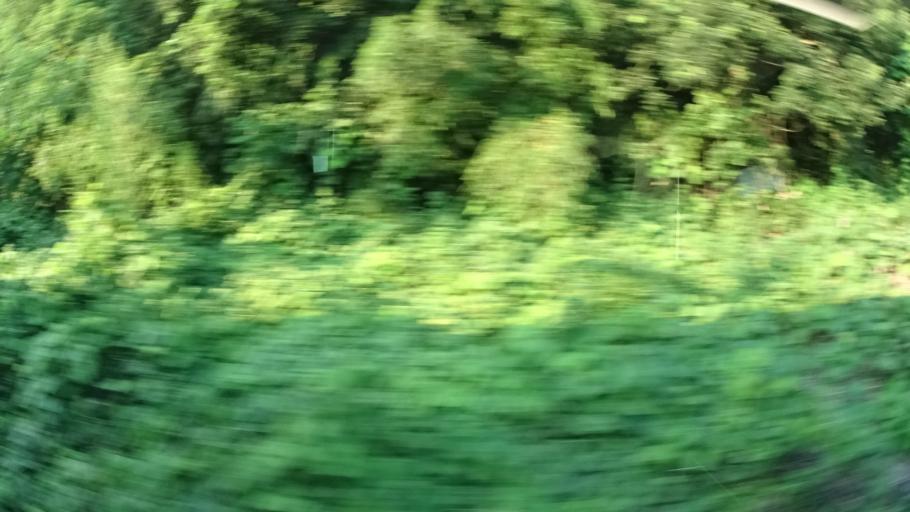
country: JP
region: Ibaraki
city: Ishioka
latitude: 36.1769
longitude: 140.2929
